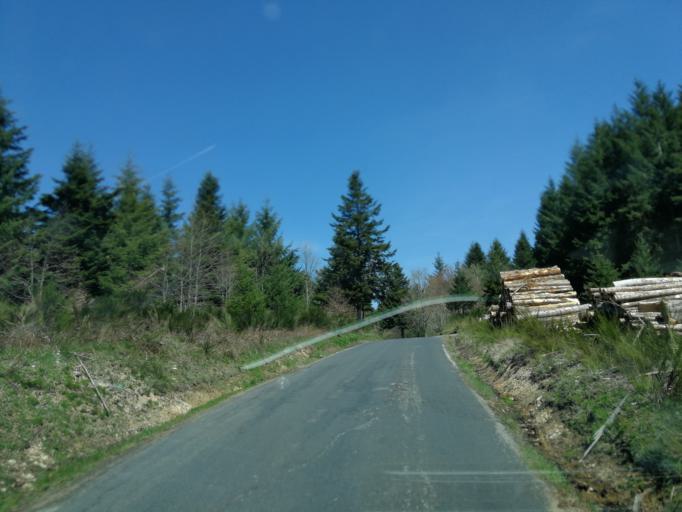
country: FR
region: Rhone-Alpes
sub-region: Departement de l'Ardeche
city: Le Cheylard
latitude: 44.9559
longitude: 4.4178
